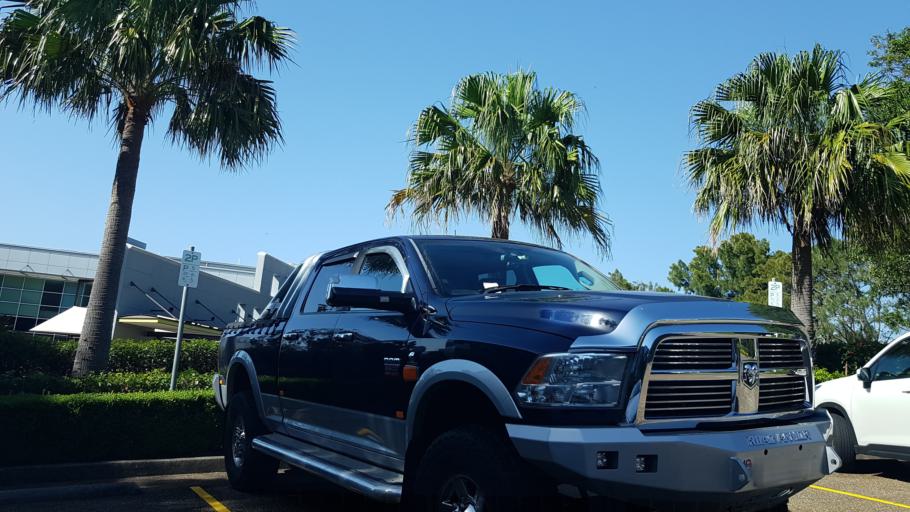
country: AU
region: New South Wales
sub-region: Warringah
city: Allambie Heights
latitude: -33.7545
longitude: 151.2484
